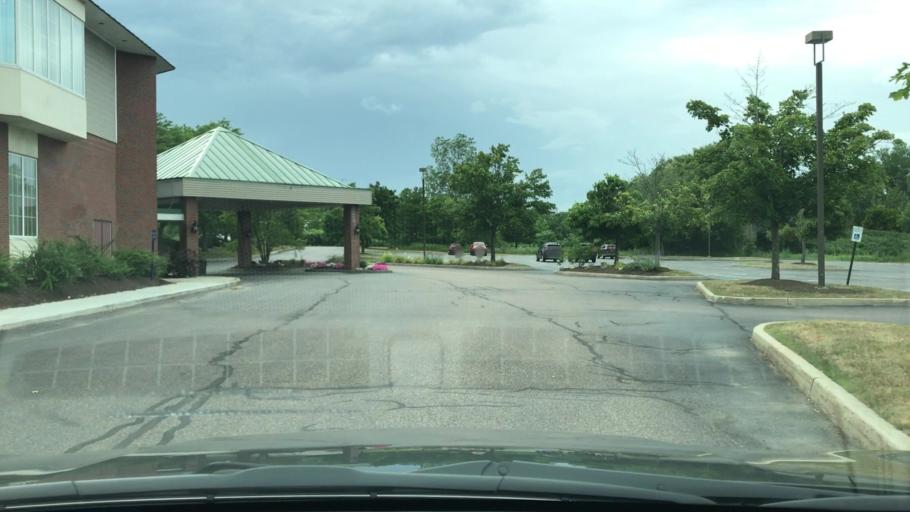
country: US
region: Vermont
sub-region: Chittenden County
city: South Burlington
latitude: 44.4728
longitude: -73.1854
